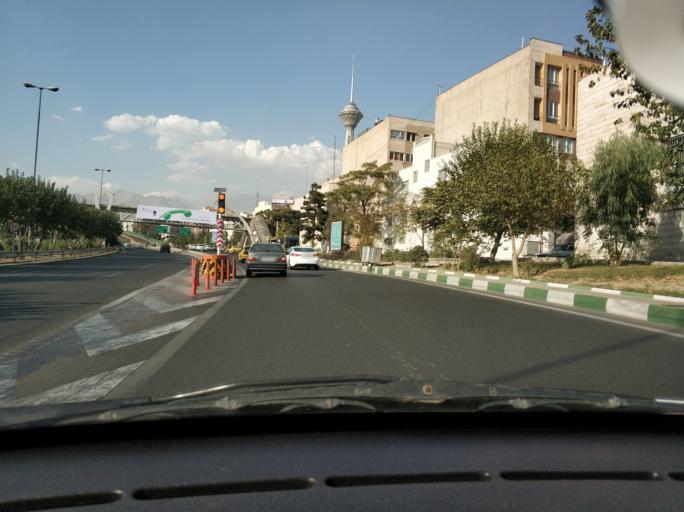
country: IR
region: Tehran
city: Tehran
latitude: 35.7331
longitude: 51.3715
